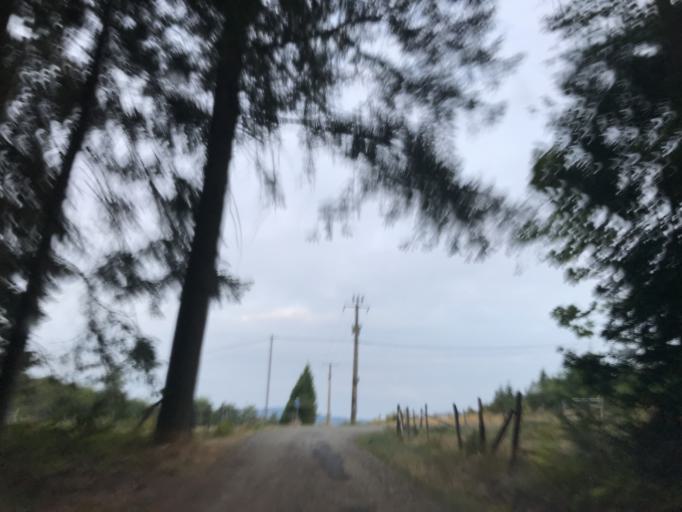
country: FR
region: Auvergne
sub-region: Departement du Puy-de-Dome
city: La Monnerie-le-Montel
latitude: 45.8507
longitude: 3.5979
